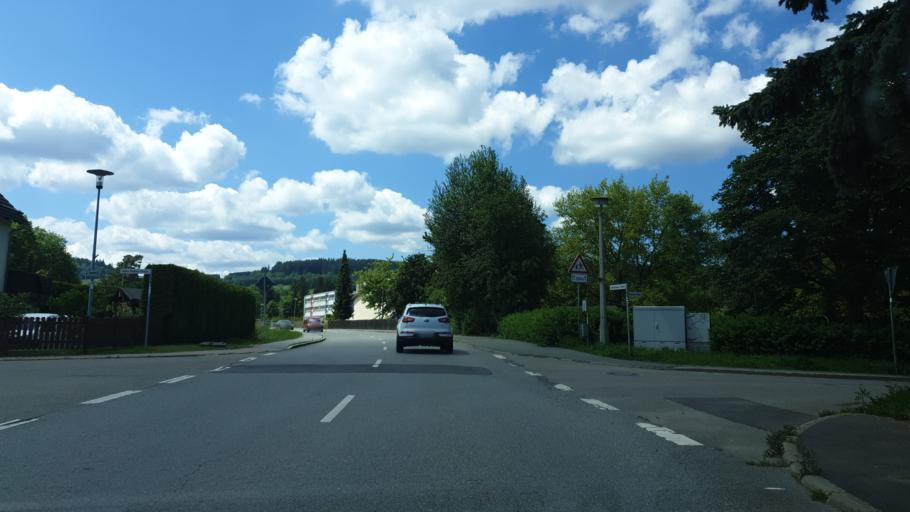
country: DE
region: Saxony
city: Schwarzenberg
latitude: 50.5360
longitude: 12.7741
